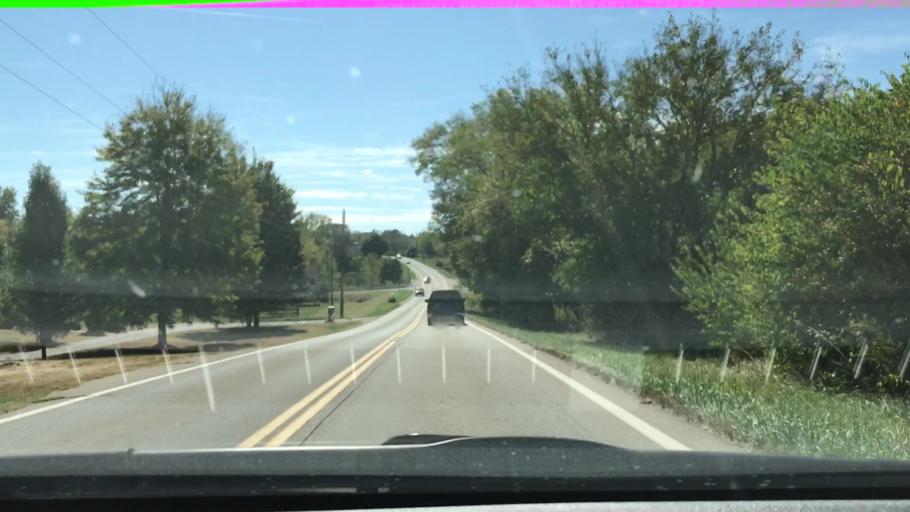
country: US
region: Ohio
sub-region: Butler County
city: Hamilton
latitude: 39.4625
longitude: -84.6282
